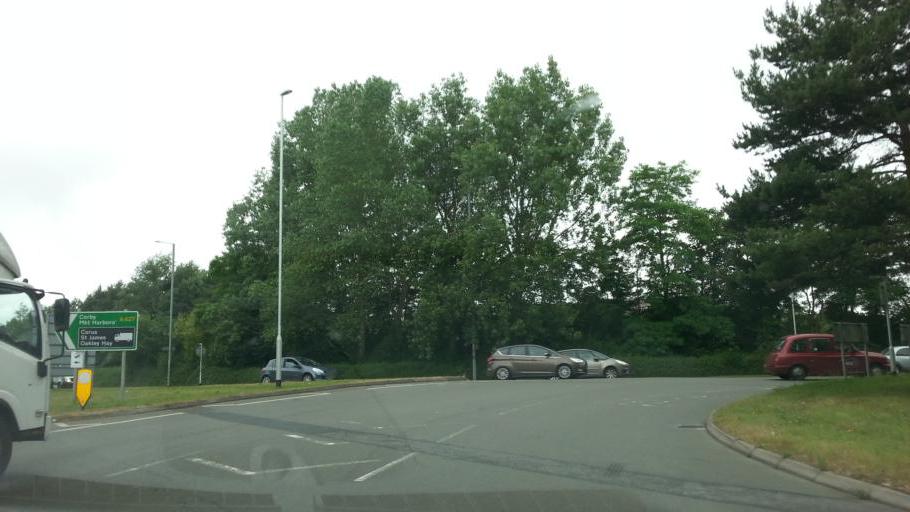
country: GB
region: England
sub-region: Northamptonshire
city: Corby
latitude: 52.4956
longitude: -0.6528
